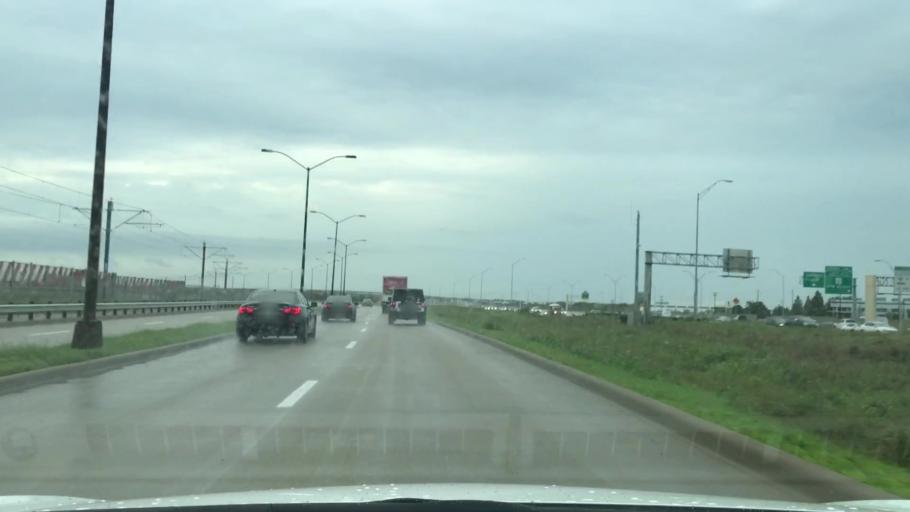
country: US
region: Texas
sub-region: Dallas County
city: Coppell
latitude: 32.9238
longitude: -97.0256
